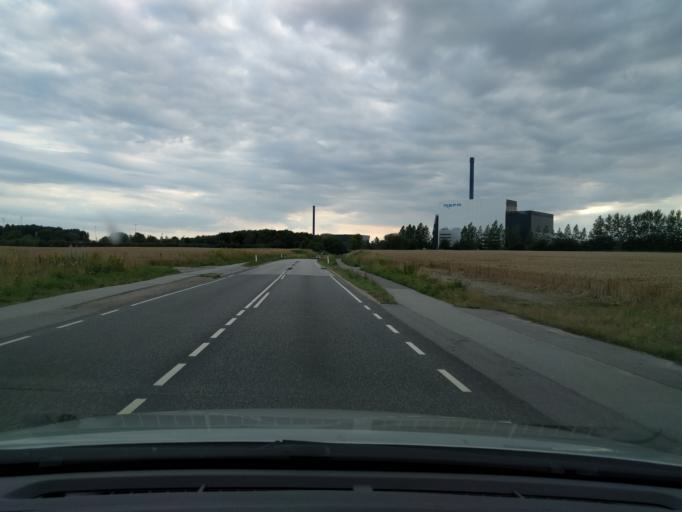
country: DK
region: Zealand
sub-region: Guldborgsund Kommune
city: Nykobing Falster
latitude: 54.7811
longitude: 11.8893
